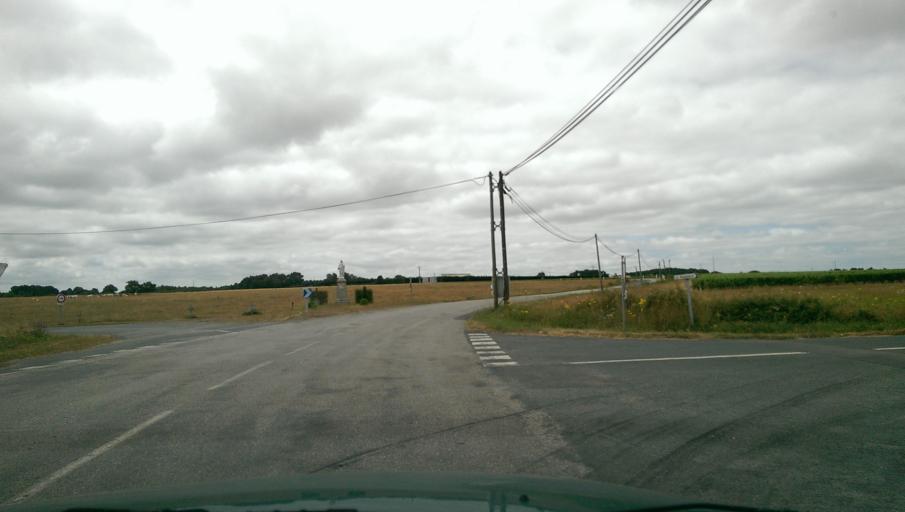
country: FR
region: Pays de la Loire
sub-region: Departement de la Loire-Atlantique
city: Remouille
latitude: 47.0506
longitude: -1.3852
